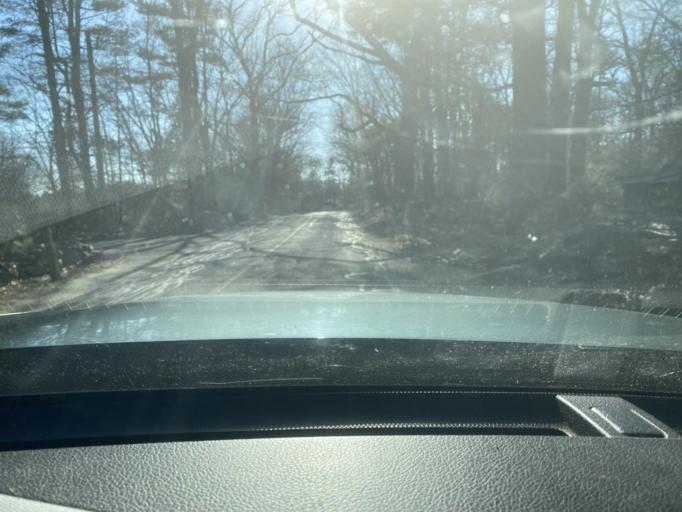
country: US
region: Massachusetts
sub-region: Middlesex County
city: Sherborn
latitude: 42.2091
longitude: -71.3885
